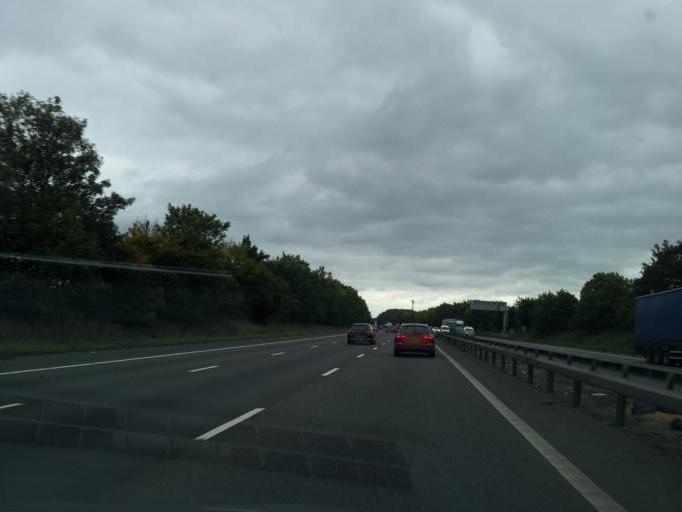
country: GB
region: England
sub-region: Northamptonshire
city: Hartwell
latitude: 52.1391
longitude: -0.8331
